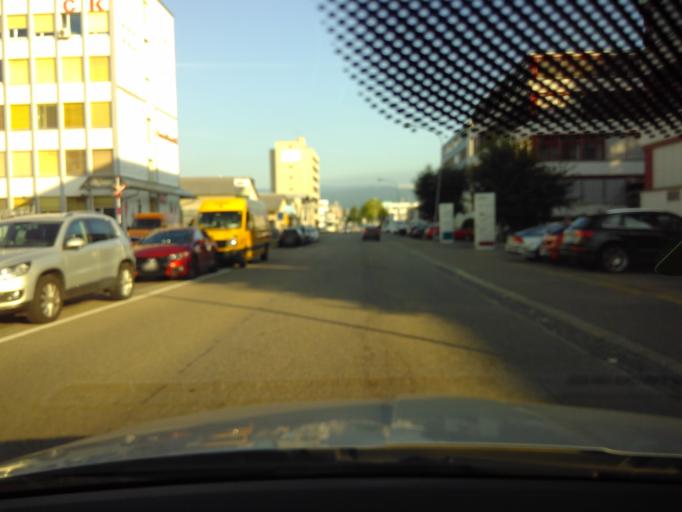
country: CH
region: Zurich
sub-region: Bezirk Dielsdorf
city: Regensdorf / Feldblumen-Riedthofstrasse
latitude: 47.4406
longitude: 8.4673
